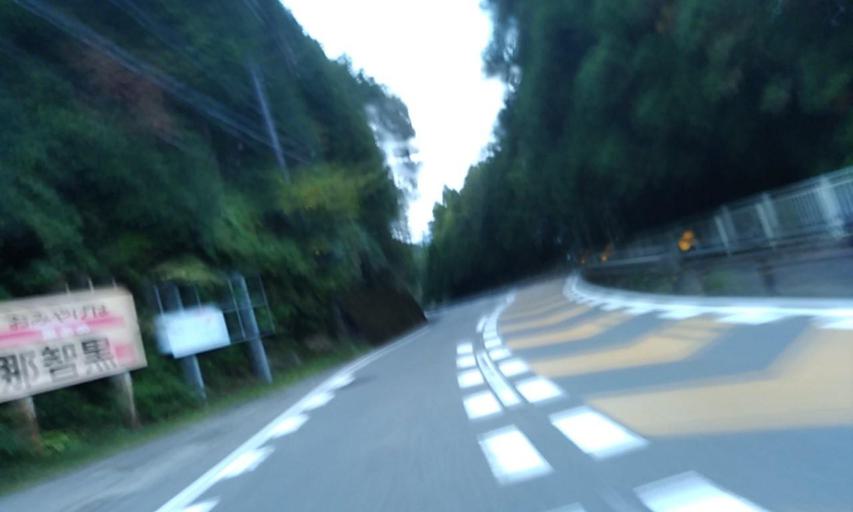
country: JP
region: Wakayama
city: Shingu
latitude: 33.7354
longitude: 135.9404
